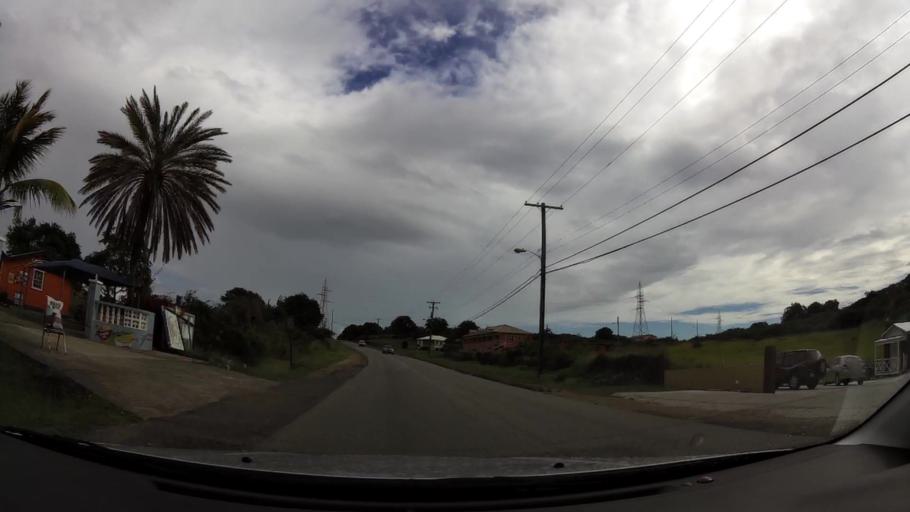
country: AG
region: Saint John
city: Potters Village
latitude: 17.0989
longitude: -61.8265
